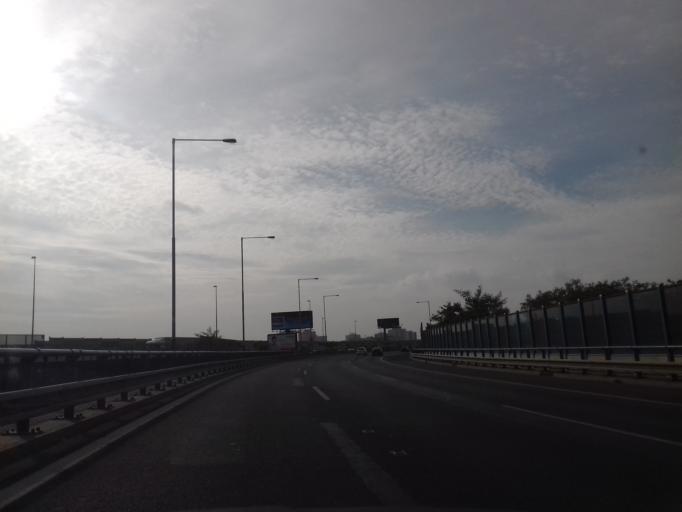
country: CZ
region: Praha
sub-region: Praha 9
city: Vysocany
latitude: 50.0653
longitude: 14.5179
